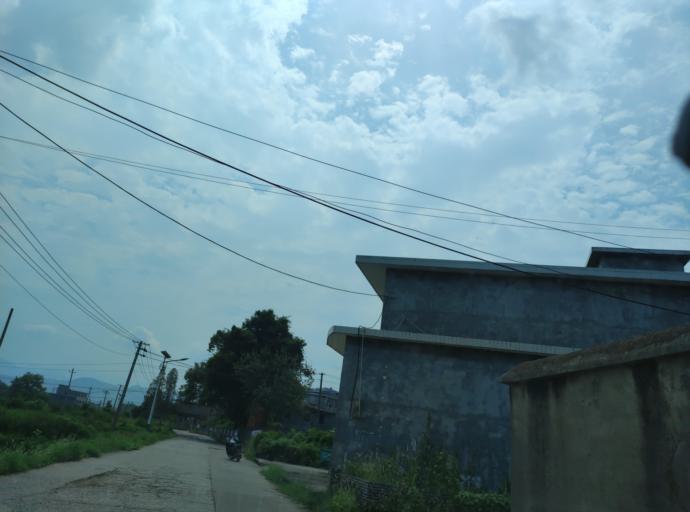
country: CN
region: Jiangxi Sheng
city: Yuannan
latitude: 27.6693
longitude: 114.0404
